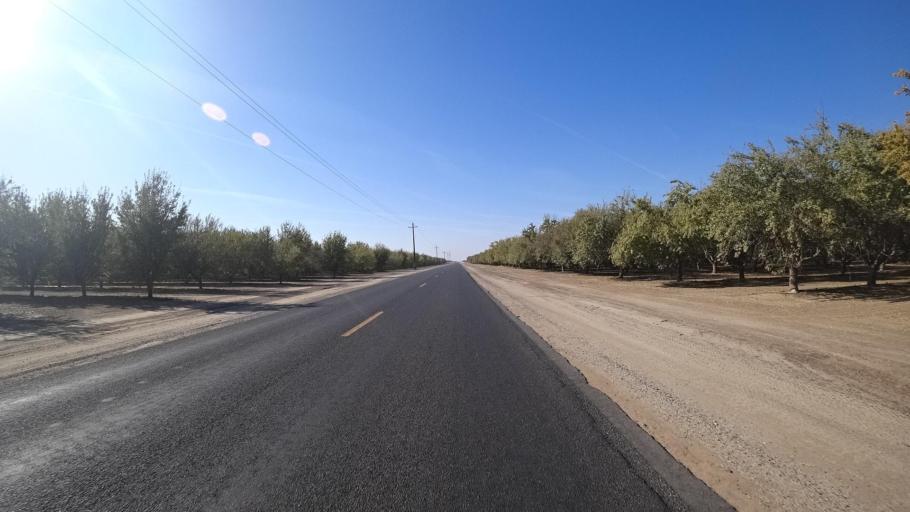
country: US
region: California
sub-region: Kern County
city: McFarland
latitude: 35.6453
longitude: -119.2713
